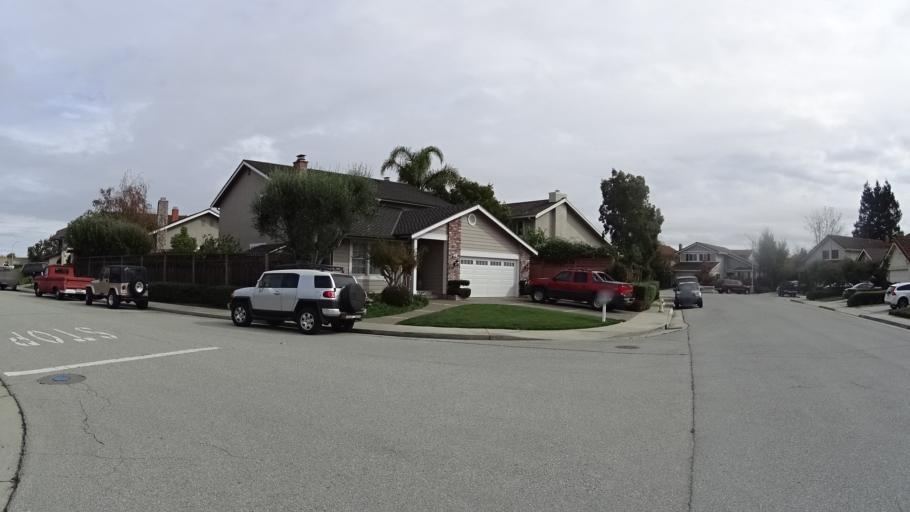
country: US
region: California
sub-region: San Mateo County
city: Belmont
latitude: 37.5301
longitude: -122.2772
